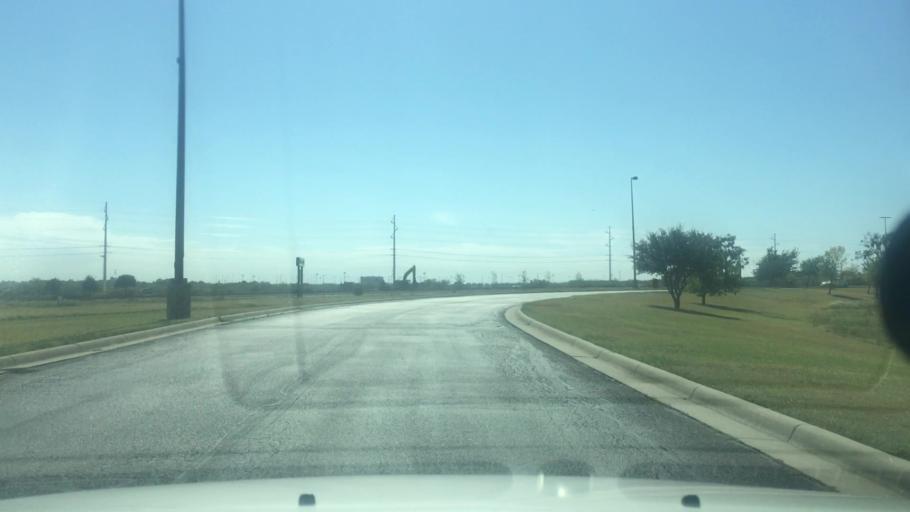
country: US
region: Texas
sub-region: Denton County
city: Denton
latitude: 33.2517
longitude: -97.1502
